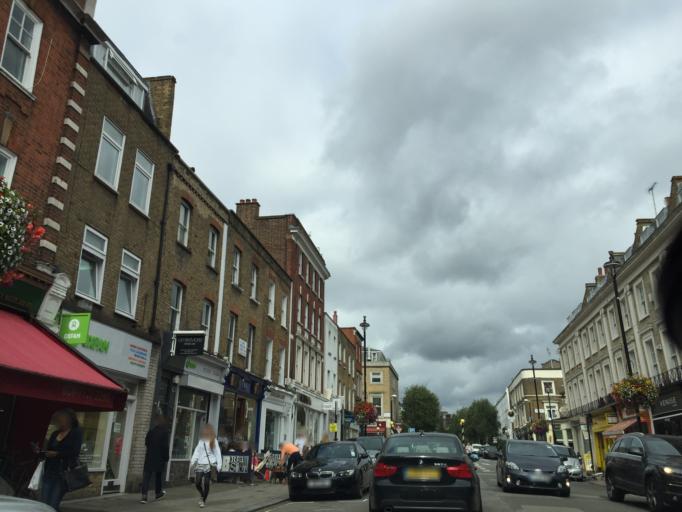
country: GB
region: England
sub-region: Greater London
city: Belsize Park
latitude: 51.5336
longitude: -0.1708
